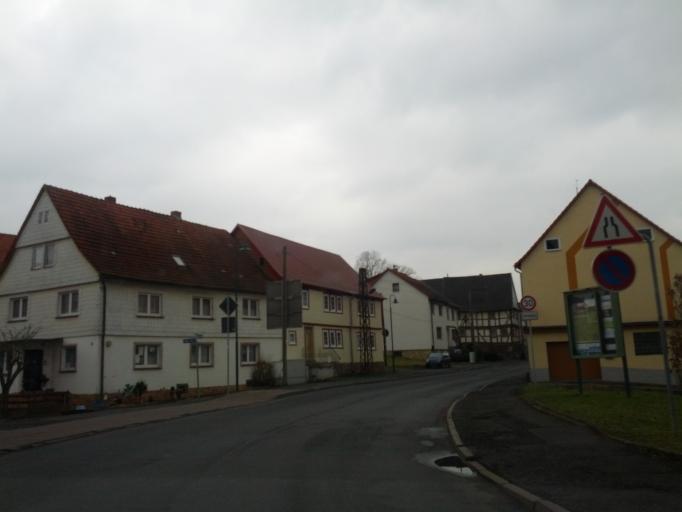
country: DE
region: Thuringia
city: Gerstungen
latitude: 50.9392
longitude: 10.0686
